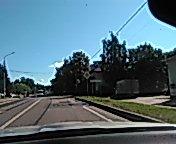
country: RU
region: Moskovskaya
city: Solnechnogorsk
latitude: 56.1827
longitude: 36.9642
